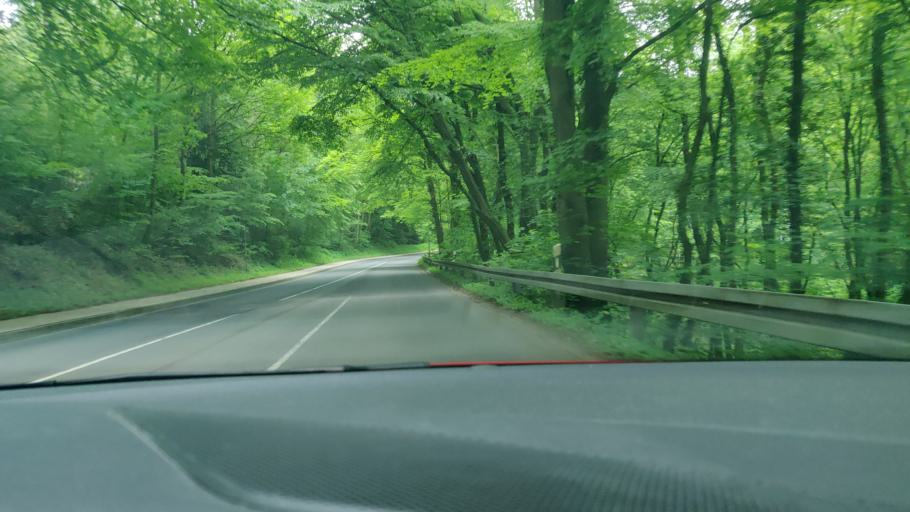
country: DE
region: North Rhine-Westphalia
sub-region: Regierungsbezirk Dusseldorf
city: Velbert
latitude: 51.3440
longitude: 7.0769
